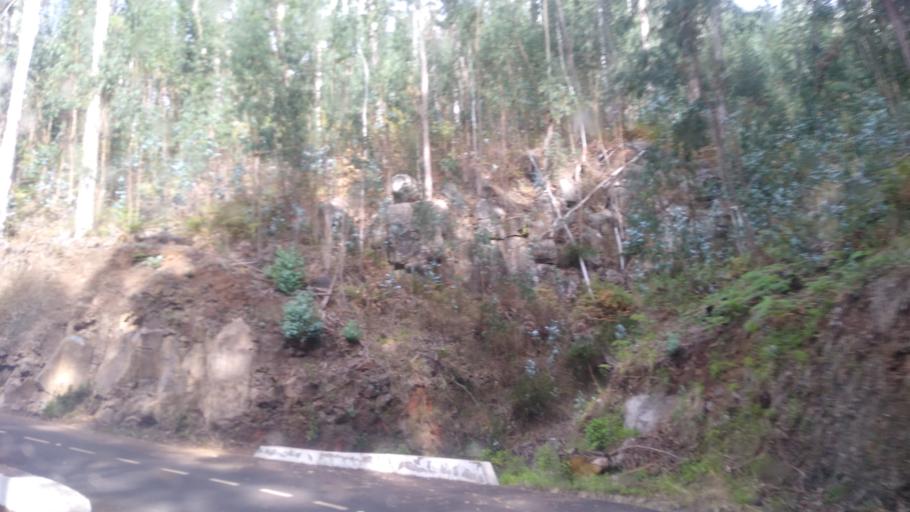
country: PT
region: Madeira
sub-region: Camara de Lobos
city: Curral das Freiras
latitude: 32.6946
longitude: -16.9398
